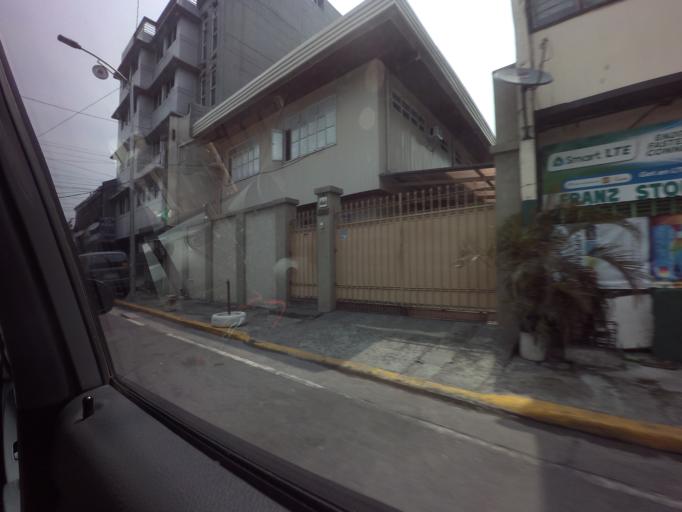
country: PH
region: Metro Manila
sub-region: City of Manila
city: Port Area
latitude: 14.5693
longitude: 120.9964
